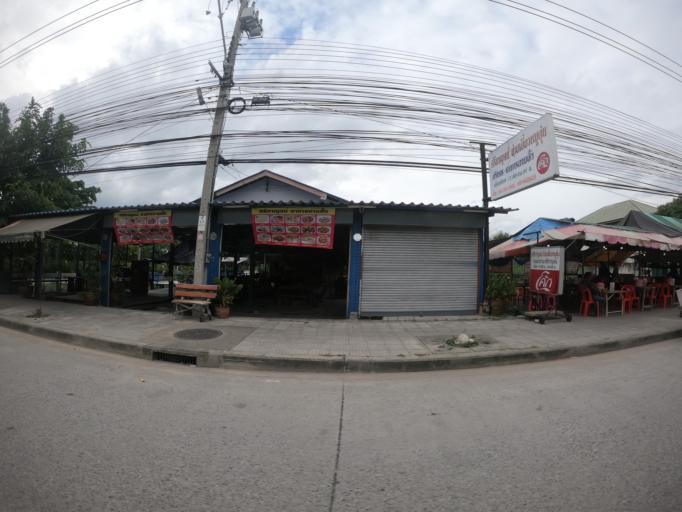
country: TH
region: Bangkok
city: Bang Na
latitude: 13.6750
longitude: 100.6783
